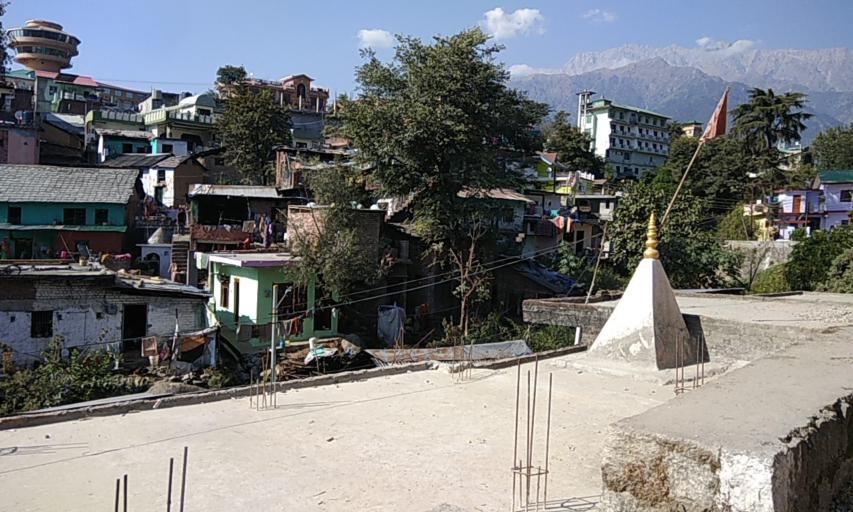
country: IN
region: Himachal Pradesh
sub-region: Kangra
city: Palampur
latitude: 32.1101
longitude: 76.5345
